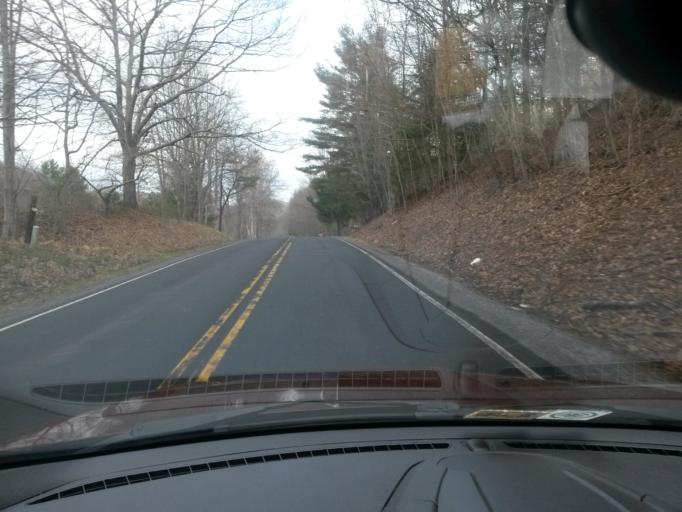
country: US
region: Virginia
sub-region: Bath County
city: Warm Springs
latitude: 38.1251
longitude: -79.7516
